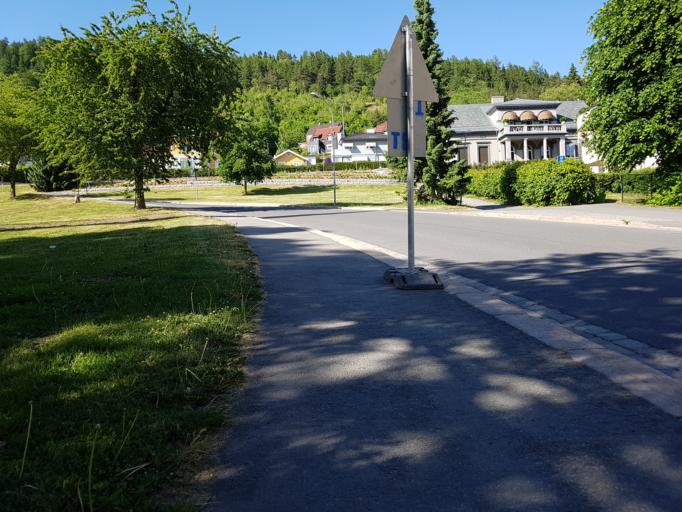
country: NO
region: Buskerud
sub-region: Drammen
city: Drammen
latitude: 59.7464
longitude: 10.2077
